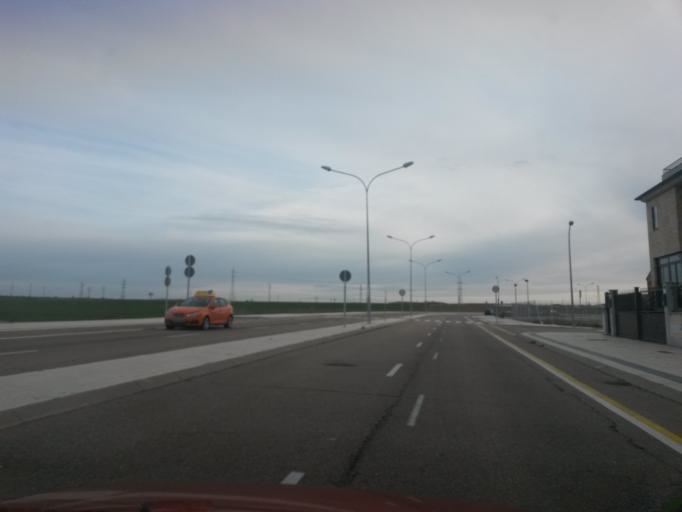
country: ES
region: Castille and Leon
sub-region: Provincia de Salamanca
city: Villares de la Reina
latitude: 41.0062
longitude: -5.6427
